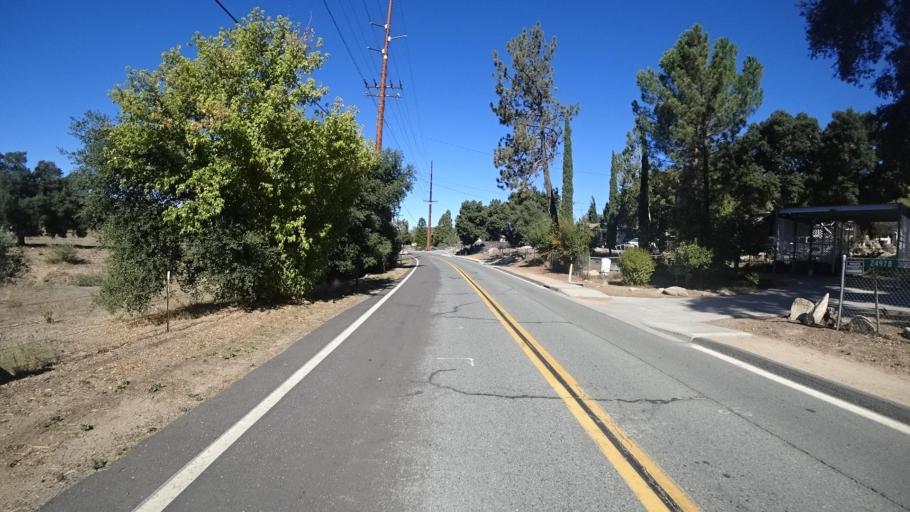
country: US
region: California
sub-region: San Diego County
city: Descanso
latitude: 32.8583
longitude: -116.6092
